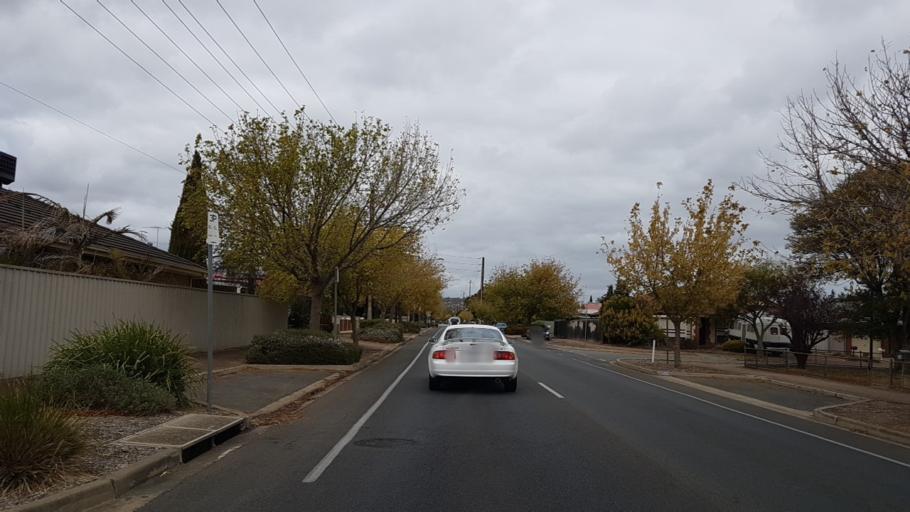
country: AU
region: South Australia
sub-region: Marion
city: Clovelly Park
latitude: -35.0062
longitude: 138.5658
